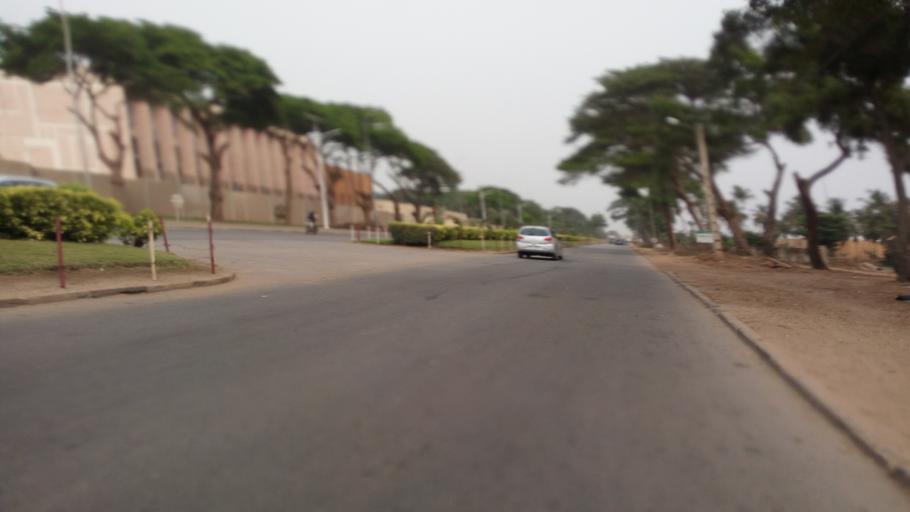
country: BJ
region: Littoral
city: Cotonou
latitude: 6.3497
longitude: 2.4079
